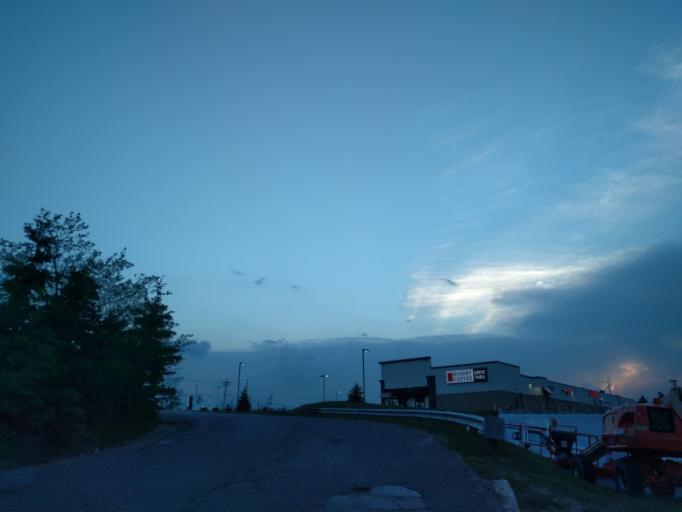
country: US
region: Michigan
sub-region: Marquette County
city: Trowbridge Park
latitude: 46.5503
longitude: -87.4550
